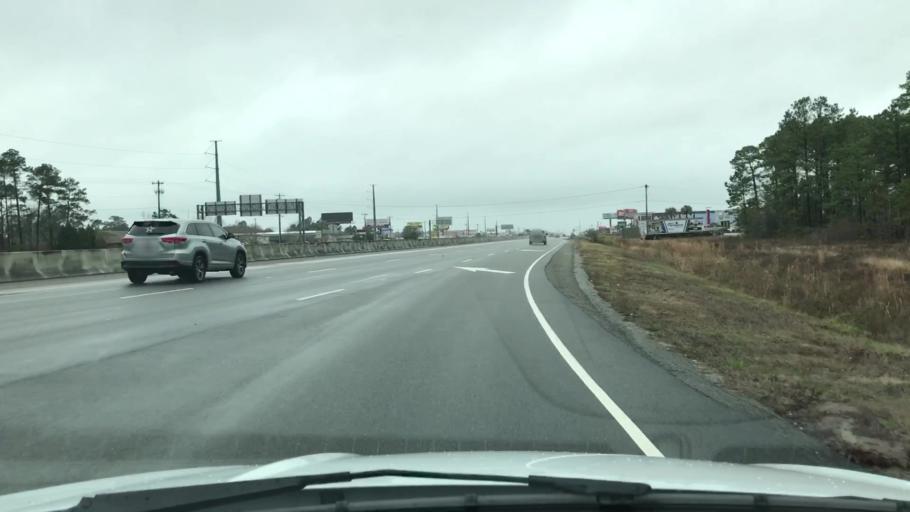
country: US
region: South Carolina
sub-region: Horry County
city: Forestbrook
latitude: 33.7428
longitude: -78.9535
